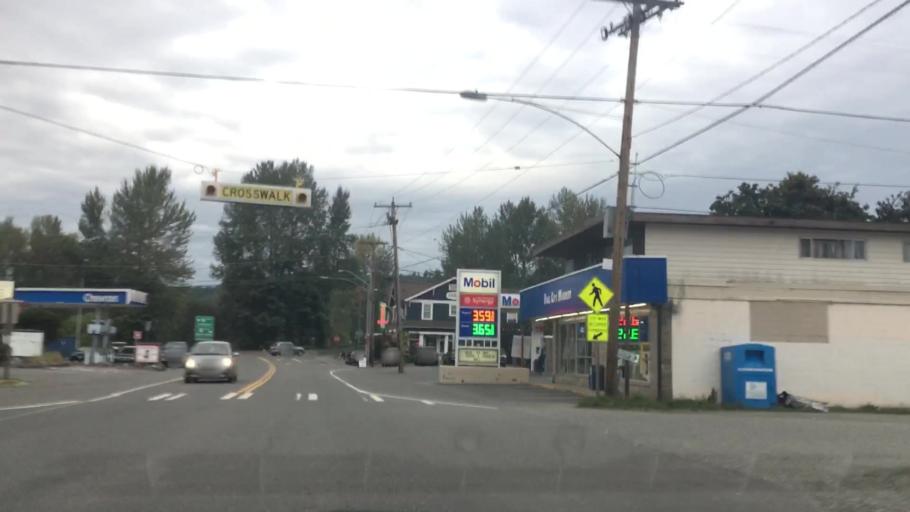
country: US
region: Washington
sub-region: King County
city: Fall City
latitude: 47.5634
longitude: -121.8900
